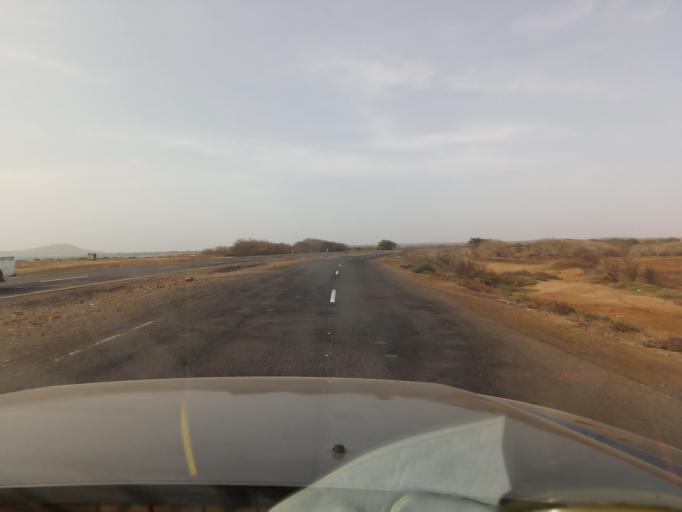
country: CV
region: Sal
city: Espargos
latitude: 16.6895
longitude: -22.9392
